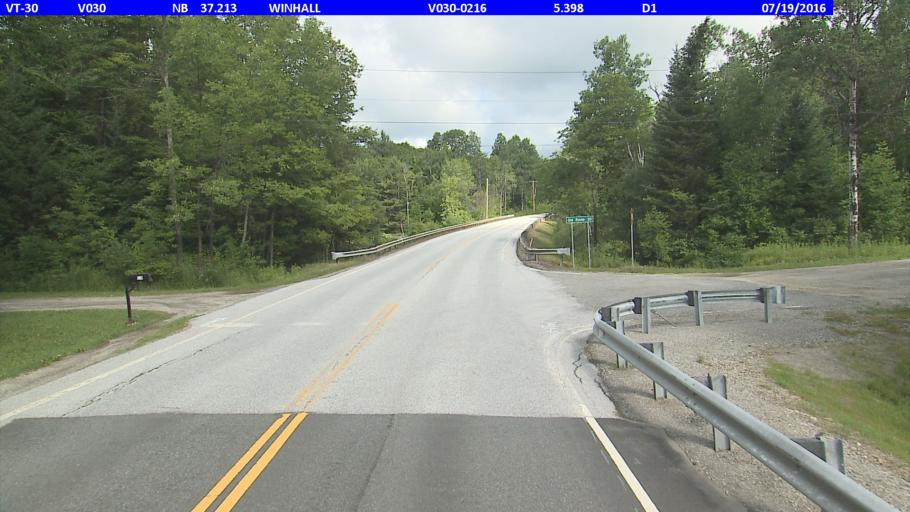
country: US
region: Vermont
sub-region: Bennington County
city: Manchester Center
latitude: 43.1848
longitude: -72.9343
